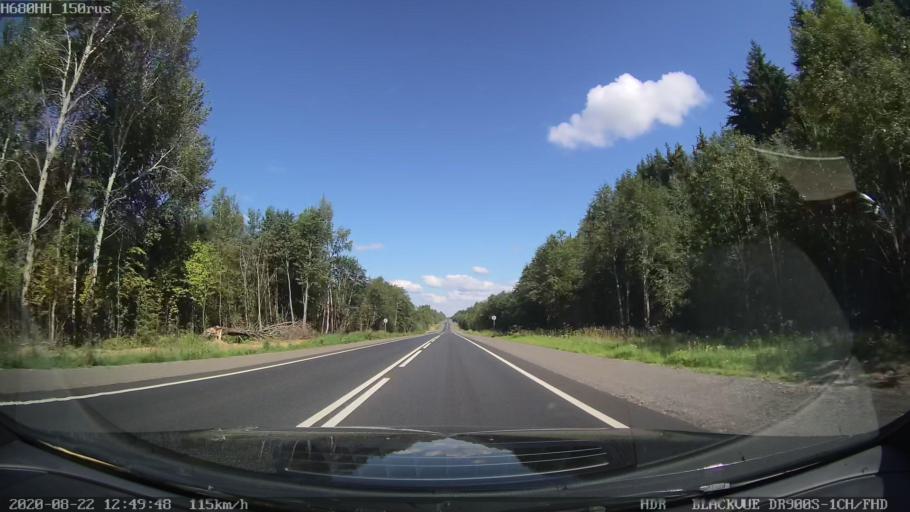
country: RU
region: Tverskaya
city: Rameshki
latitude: 57.4568
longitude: 36.2116
